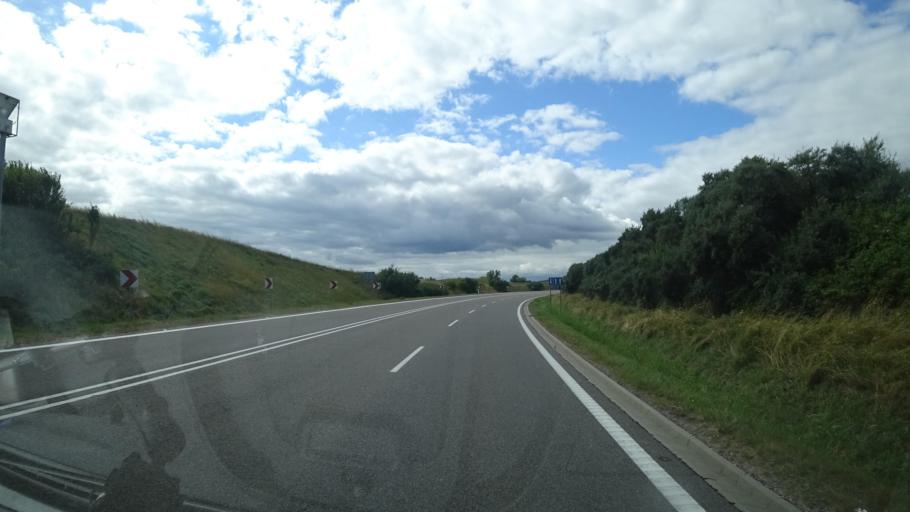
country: PL
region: Warmian-Masurian Voivodeship
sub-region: Powiat goldapski
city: Goldap
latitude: 54.2978
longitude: 22.2846
